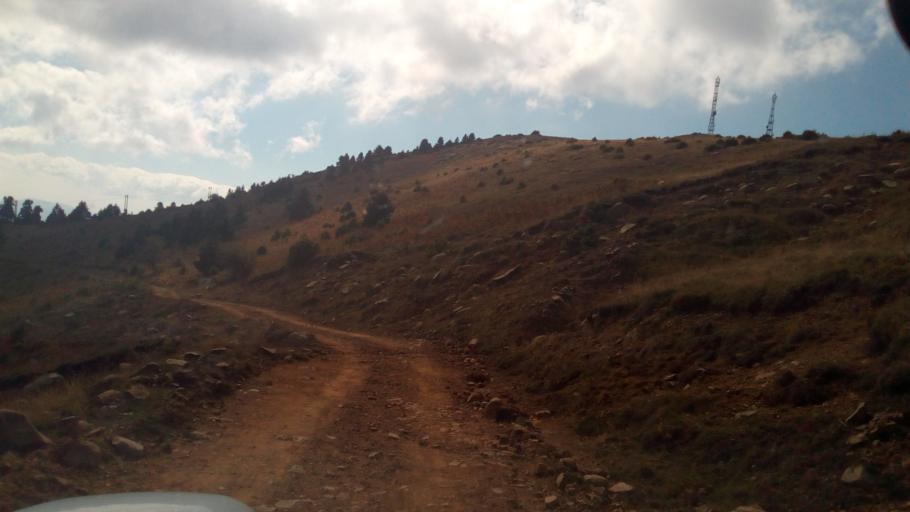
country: GR
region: Central Greece
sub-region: Nomos Fokidos
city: Lidoriki
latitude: 38.6079
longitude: 21.9674
